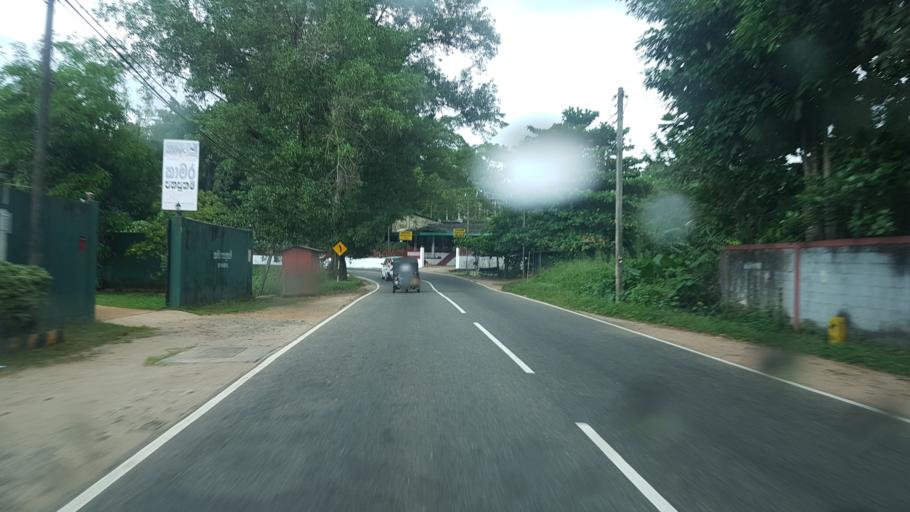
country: LK
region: Western
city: Hanwella Ihala
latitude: 6.9656
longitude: 80.2318
